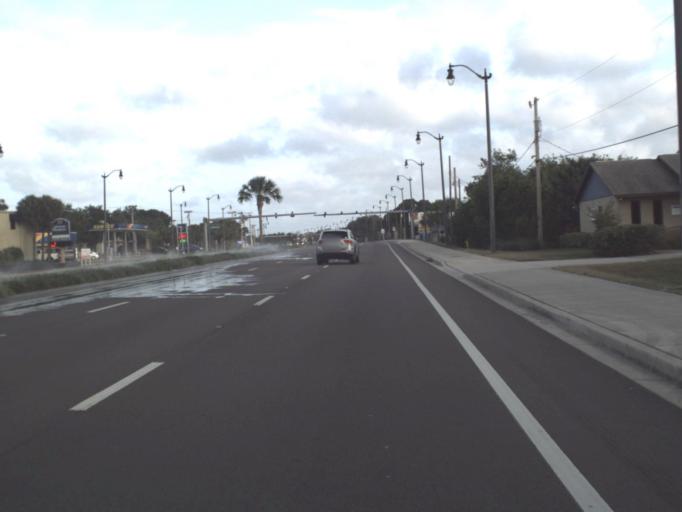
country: US
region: Florida
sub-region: Brevard County
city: Rockledge
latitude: 28.3390
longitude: -80.7272
